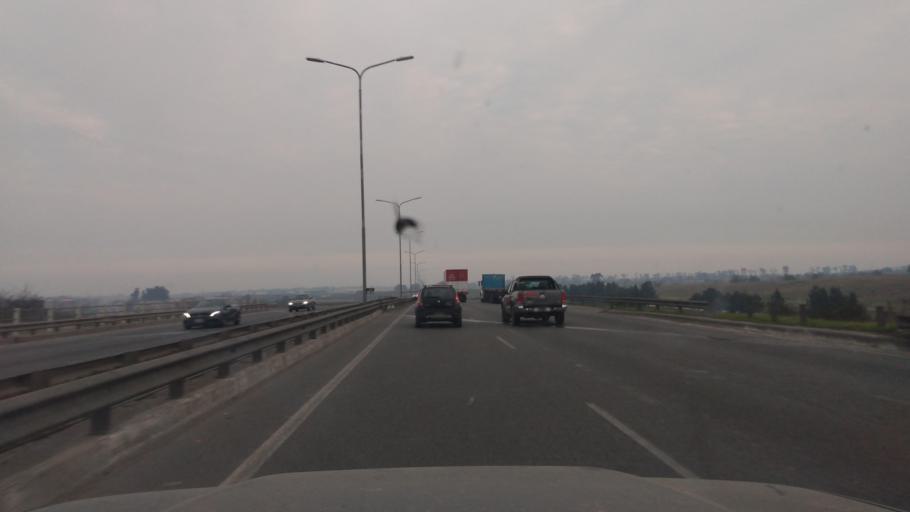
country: AR
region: Buenos Aires
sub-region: Partido de Tigre
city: Tigre
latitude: -34.5096
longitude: -58.5901
